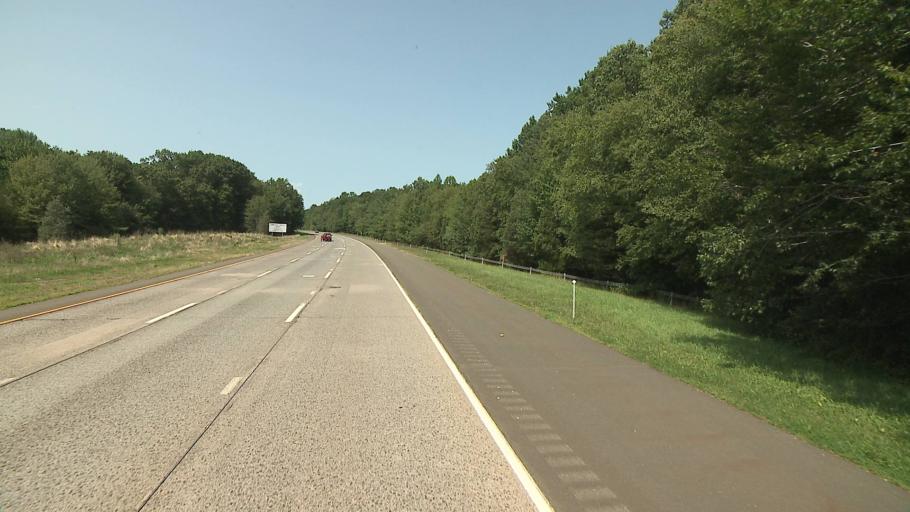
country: US
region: Connecticut
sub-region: Fairfield County
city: Trumbull
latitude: 41.2750
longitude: -73.2115
